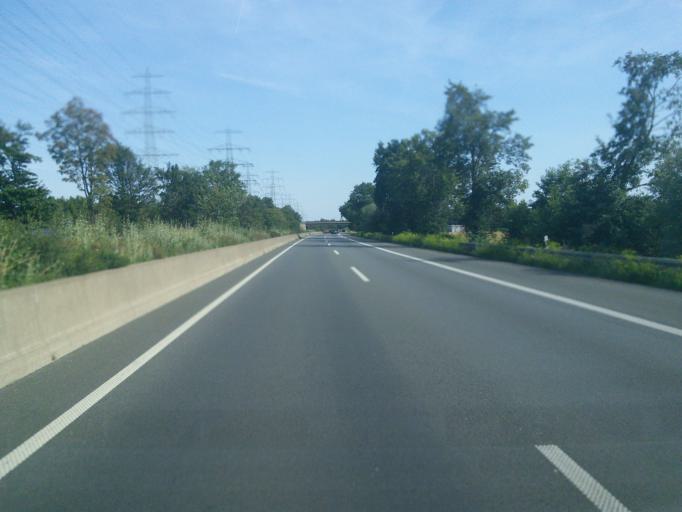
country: DE
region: North Rhine-Westphalia
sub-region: Regierungsbezirk Dusseldorf
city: Dormagen
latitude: 51.1356
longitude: 6.7835
